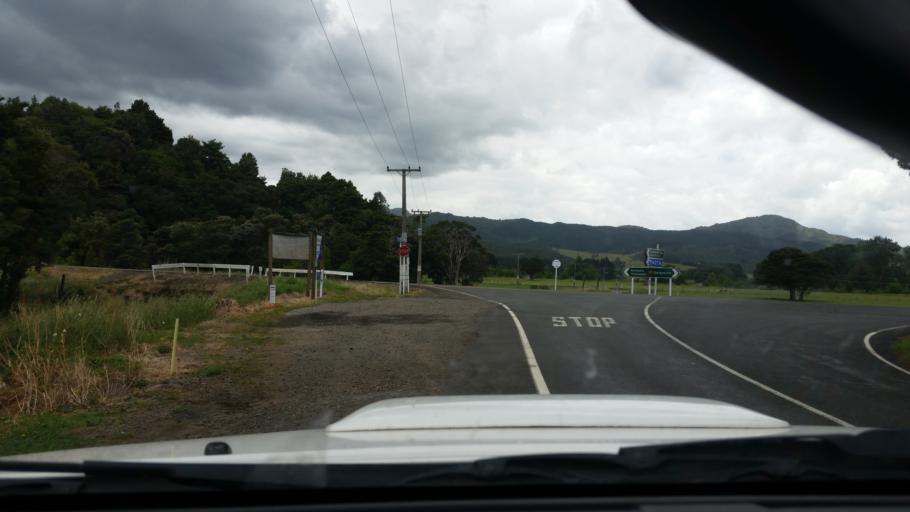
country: NZ
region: Northland
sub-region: Kaipara District
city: Dargaville
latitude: -35.8102
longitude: 173.7282
